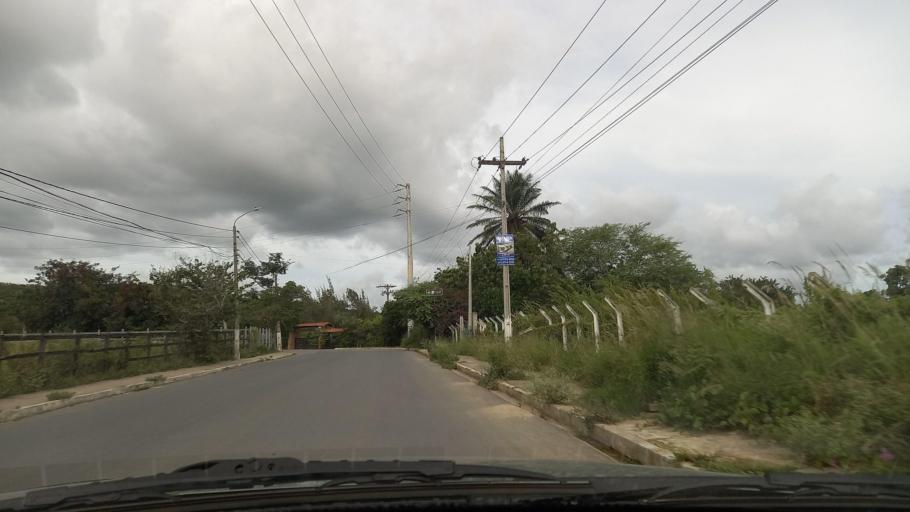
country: BR
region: Pernambuco
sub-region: Gravata
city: Gravata
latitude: -8.2065
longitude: -35.5577
